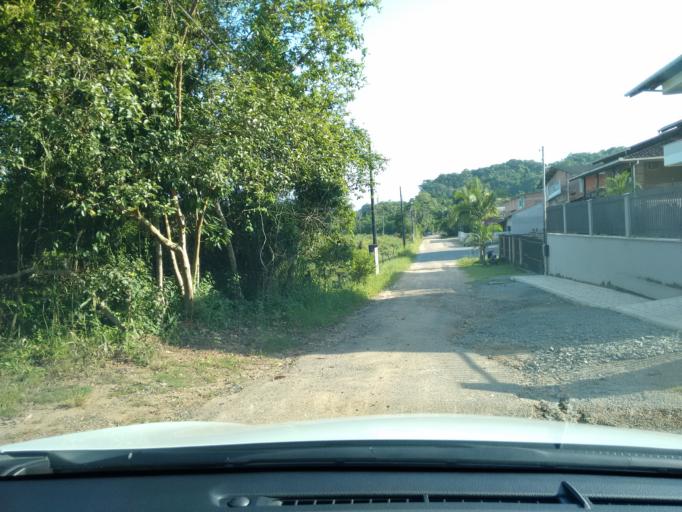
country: BR
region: Santa Catarina
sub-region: Blumenau
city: Blumenau
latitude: -26.8587
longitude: -49.1002
